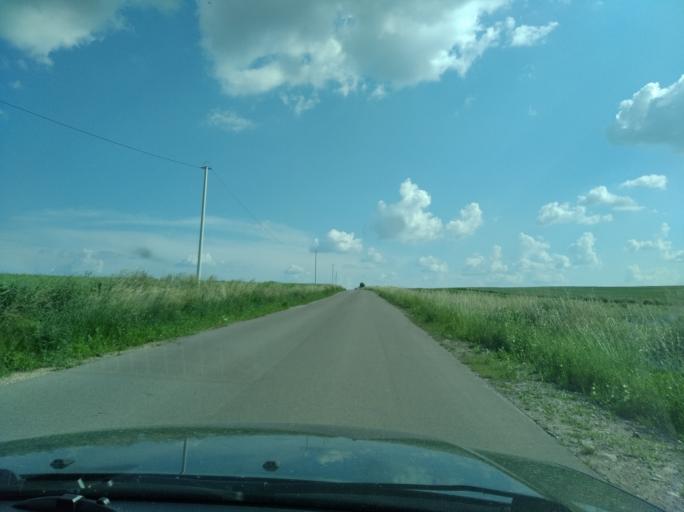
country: PL
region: Subcarpathian Voivodeship
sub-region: Powiat jaroslawski
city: Ostrow
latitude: 49.9354
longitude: 22.7399
